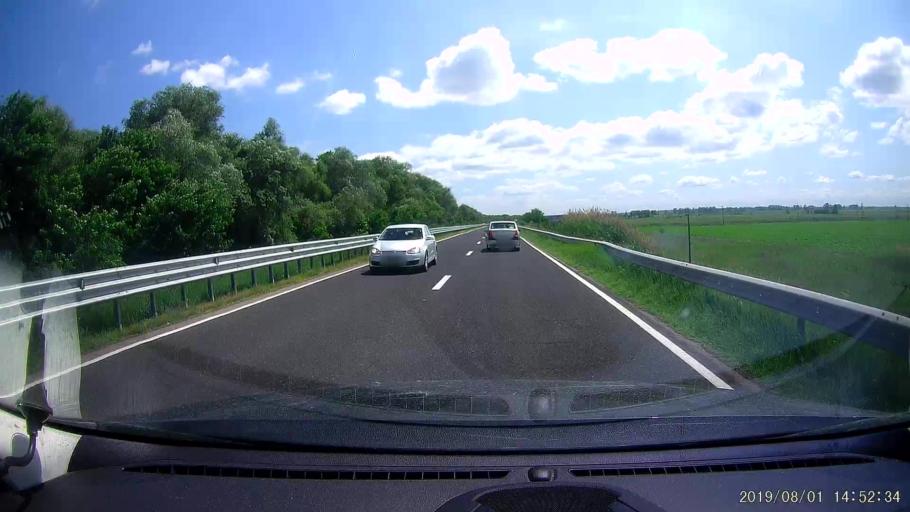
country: RO
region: Braila
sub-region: Comuna Vadeni
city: Vadeni
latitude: 45.3525
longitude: 28.0102
